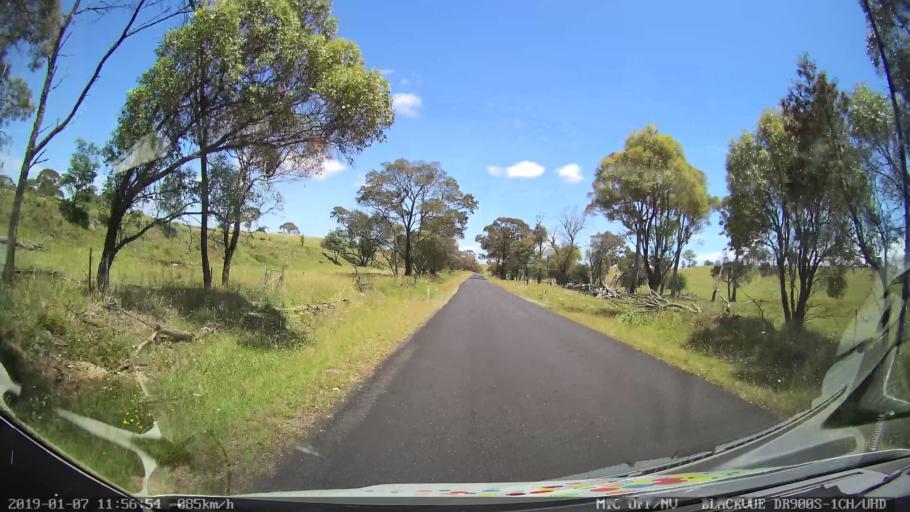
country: AU
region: New South Wales
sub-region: Guyra
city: Guyra
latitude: -30.2700
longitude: 151.6697
